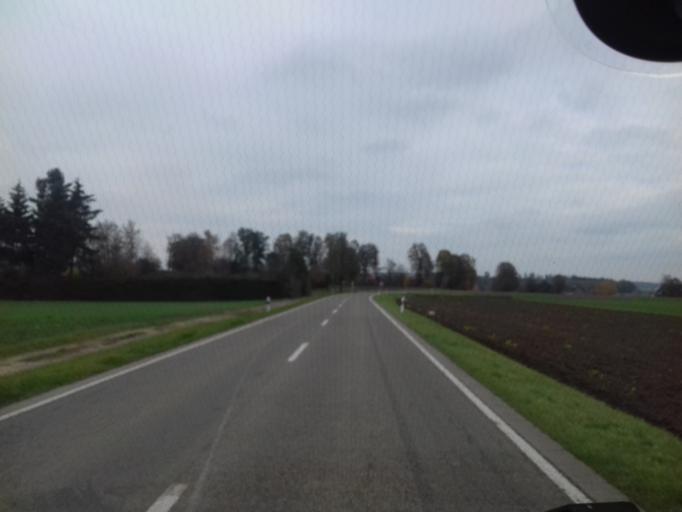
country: DE
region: Bavaria
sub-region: Swabia
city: Ziertheim
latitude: 48.6673
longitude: 10.3664
